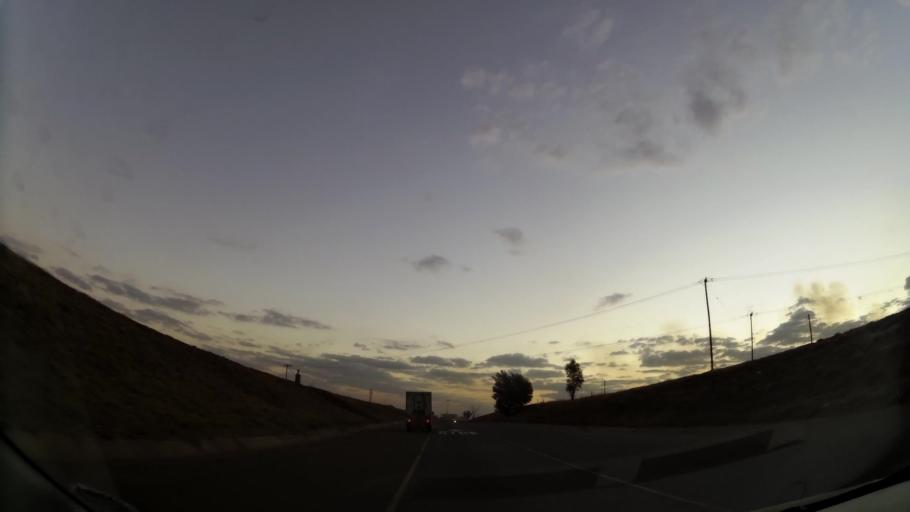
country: ZA
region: Gauteng
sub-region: West Rand District Municipality
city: Randfontein
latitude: -26.0735
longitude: 27.6520
